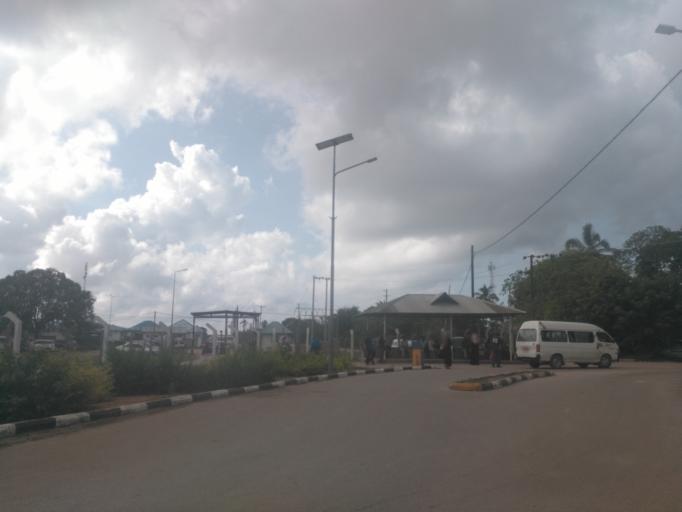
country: TZ
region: Zanzibar Urban/West
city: Zanzibar
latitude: -6.2174
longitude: 39.2200
